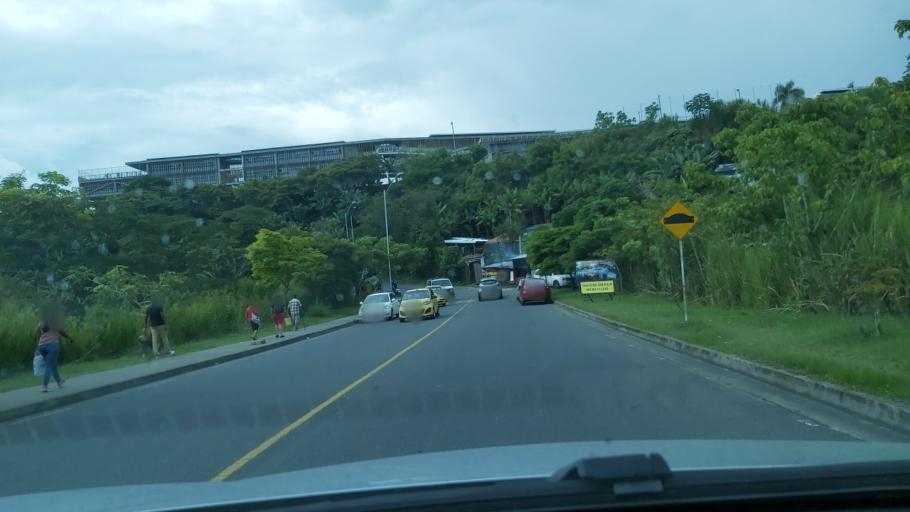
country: CO
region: Risaralda
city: Pereira
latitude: 4.7948
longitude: -75.7104
